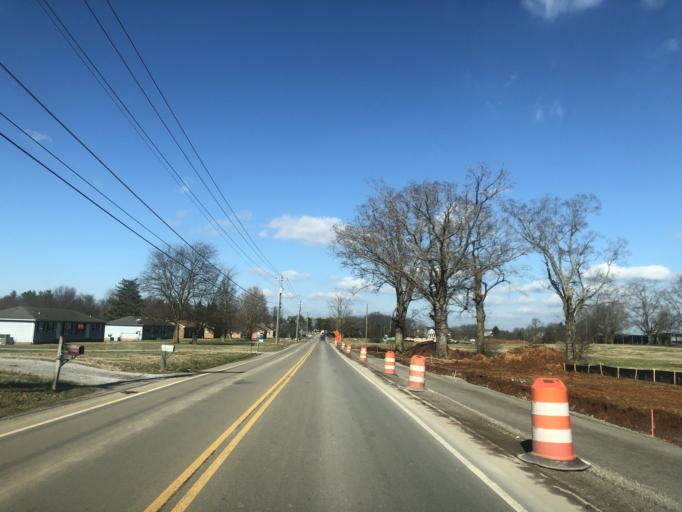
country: US
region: Tennessee
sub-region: Rutherford County
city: Smyrna
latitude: 35.8808
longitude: -86.4967
